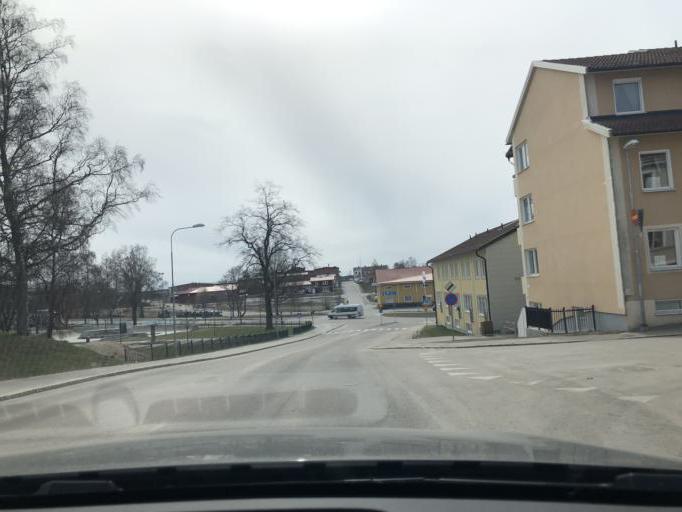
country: SE
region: Gaevleborg
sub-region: Hudiksvalls Kommun
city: Hudiksvall
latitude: 61.7276
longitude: 17.1223
